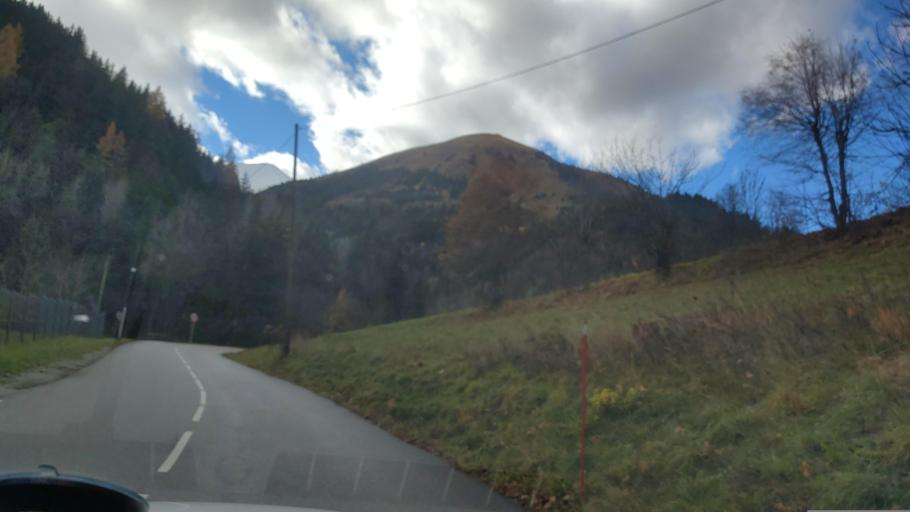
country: FR
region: Rhone-Alpes
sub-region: Departement de la Savoie
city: Saint-Jean-de-Maurienne
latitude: 45.1929
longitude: 6.2900
